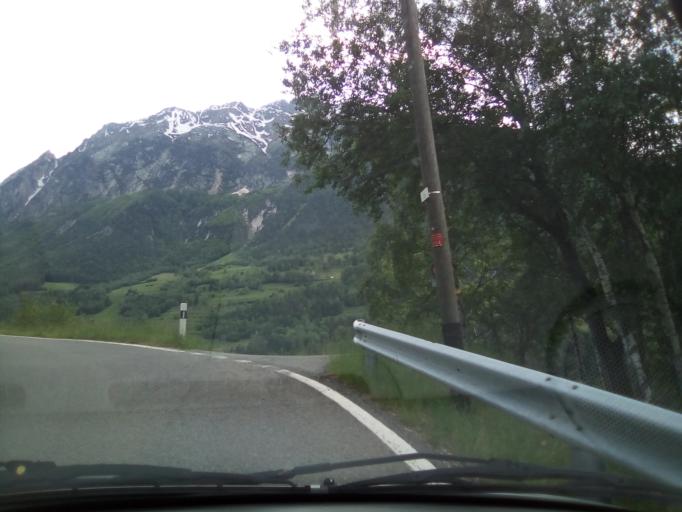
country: CH
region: Valais
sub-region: Entremont District
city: Orsieres
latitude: 46.0639
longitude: 7.1549
